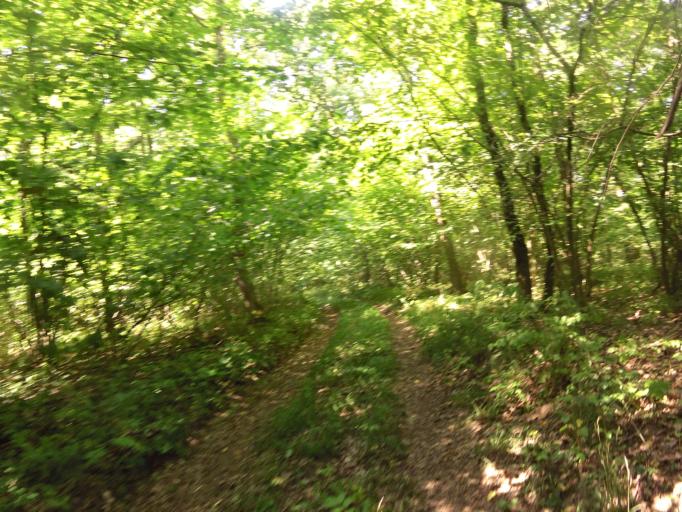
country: DE
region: Bavaria
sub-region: Regierungsbezirk Unterfranken
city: Rimpar
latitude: 49.8263
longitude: 9.9534
